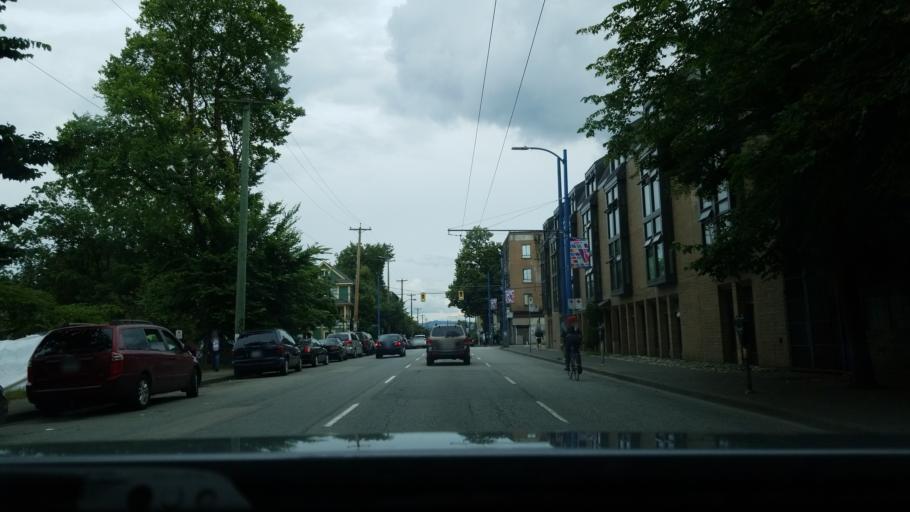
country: CA
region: British Columbia
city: West End
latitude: 49.2822
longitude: -123.0945
